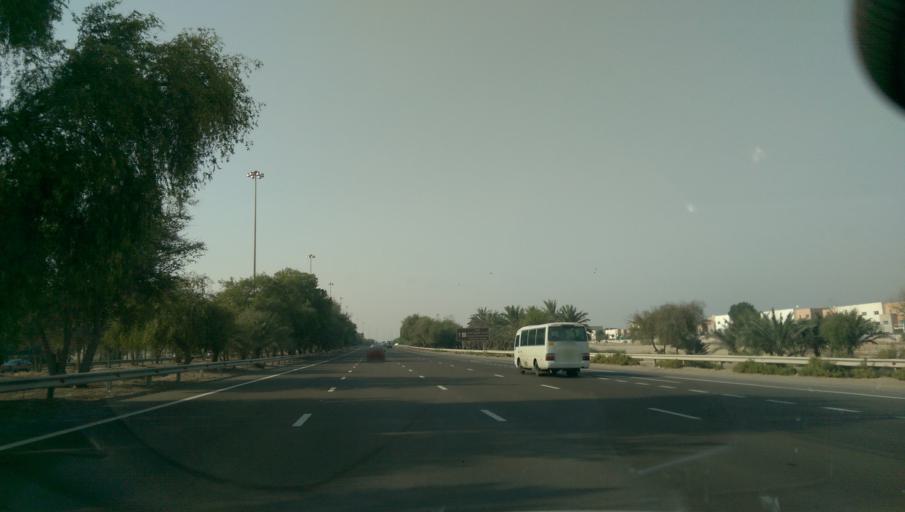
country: AE
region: Abu Dhabi
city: Abu Dhabi
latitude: 24.4589
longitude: 54.6778
